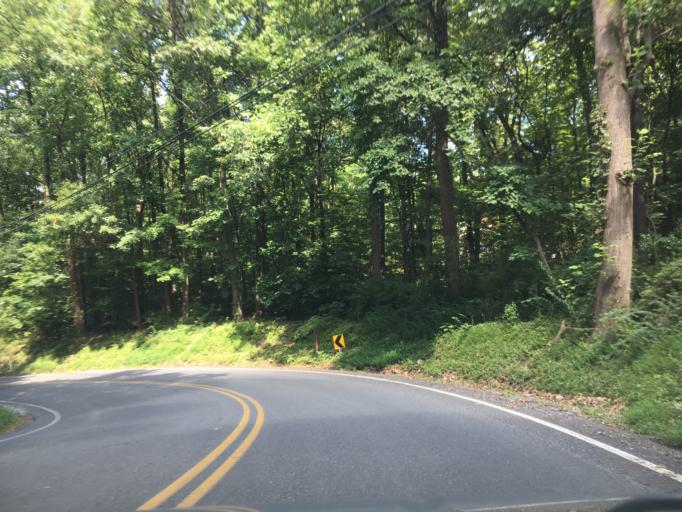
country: US
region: Pennsylvania
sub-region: Berks County
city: Fleetwood
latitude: 40.4462
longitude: -75.8090
